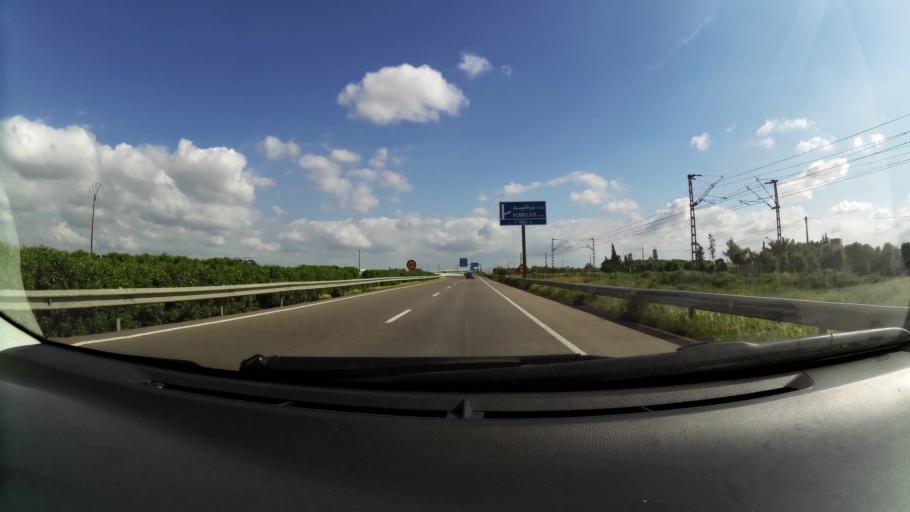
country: MA
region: Chaouia-Ouardigha
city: Nouaseur
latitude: 33.3299
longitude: -7.6082
